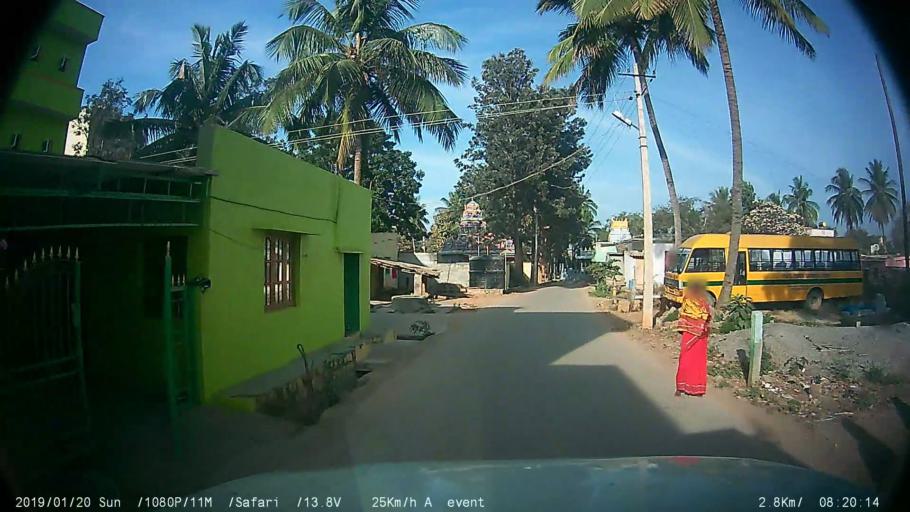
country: IN
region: Karnataka
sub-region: Bangalore Urban
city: Anekal
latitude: 12.8177
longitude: 77.6380
